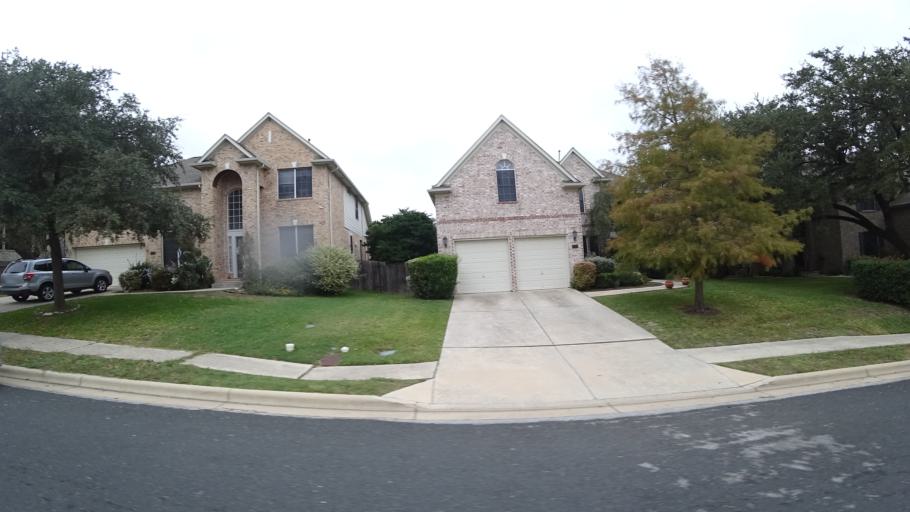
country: US
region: Texas
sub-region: Williamson County
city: Anderson Mill
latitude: 30.4371
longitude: -97.8179
